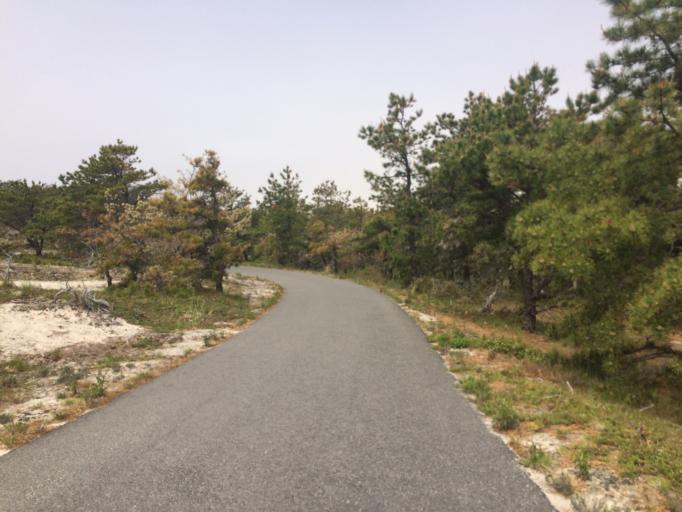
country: US
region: Massachusetts
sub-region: Barnstable County
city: Provincetown
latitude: 42.0751
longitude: -70.2029
